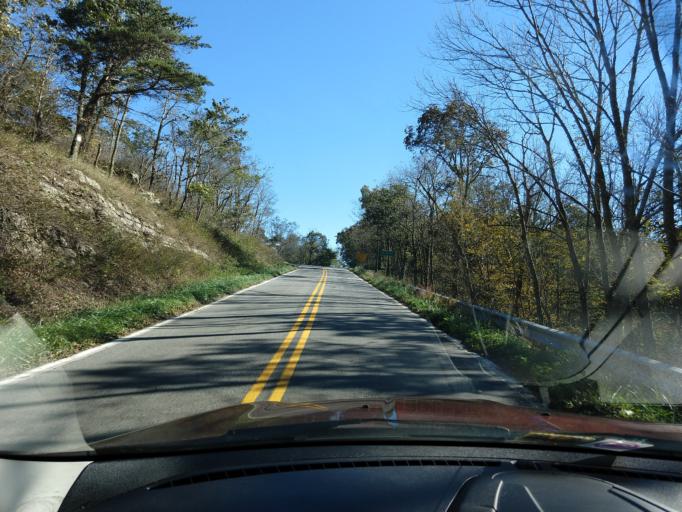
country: US
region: Virginia
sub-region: Alleghany County
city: Clifton Forge
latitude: 37.8763
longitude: -79.8880
